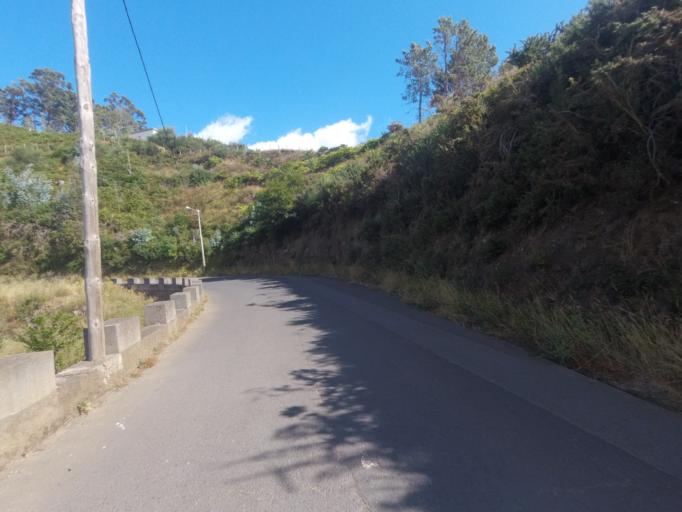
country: PT
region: Madeira
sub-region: Ribeira Brava
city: Campanario
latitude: 32.6998
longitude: -17.0171
